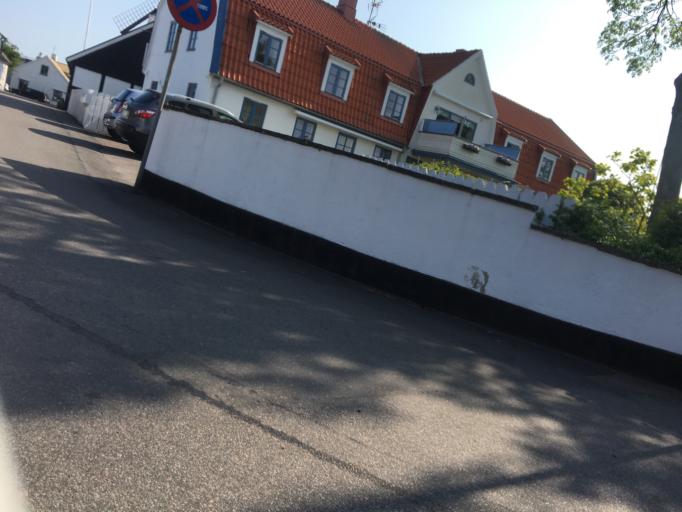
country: SE
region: Skane
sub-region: Hoganas Kommun
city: Hoganas
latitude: 56.1441
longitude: 12.5769
